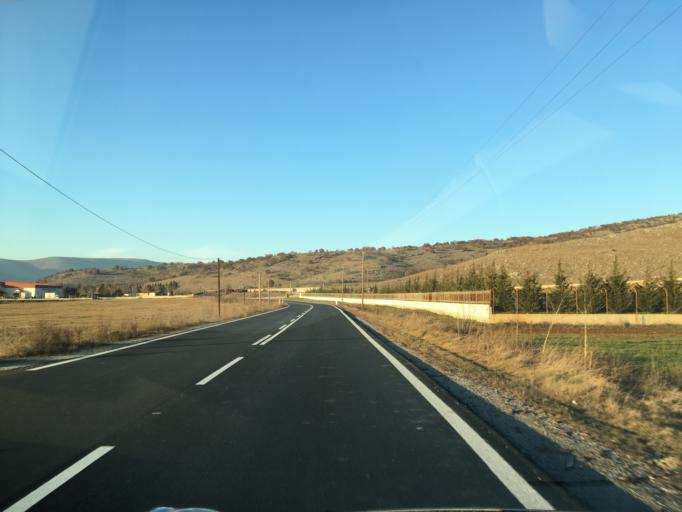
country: GR
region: West Macedonia
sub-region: Nomos Kozanis
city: Kozani
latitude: 40.3016
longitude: 21.7360
